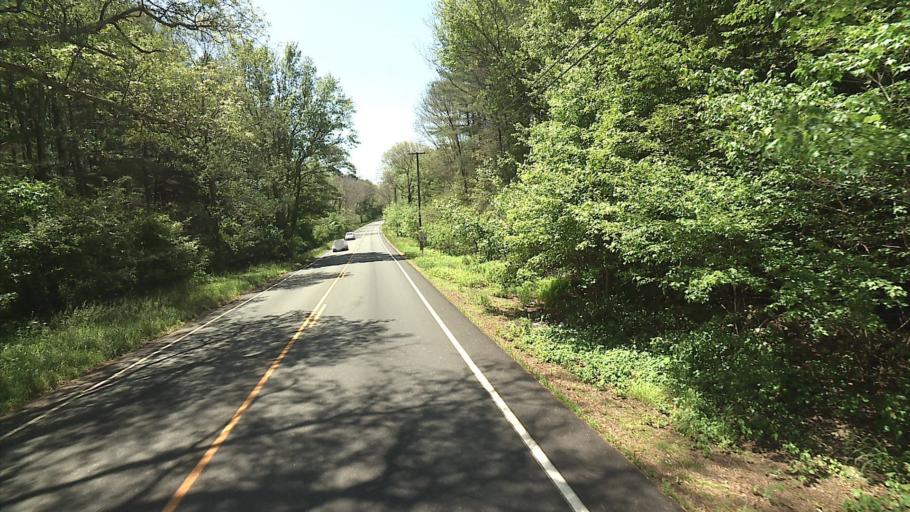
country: US
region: Connecticut
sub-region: Windham County
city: Plainfield
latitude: 41.6172
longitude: -71.8426
